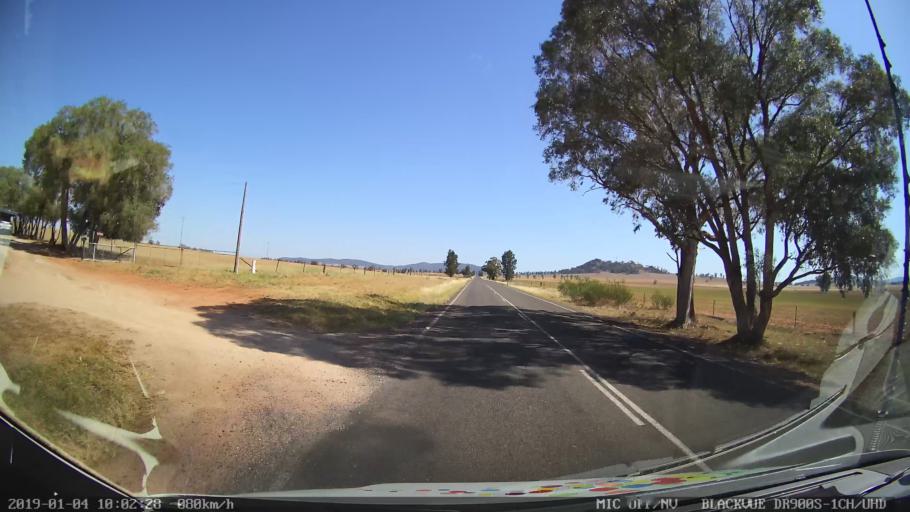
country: AU
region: New South Wales
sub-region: Cabonne
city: Canowindra
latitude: -33.4758
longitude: 148.3654
